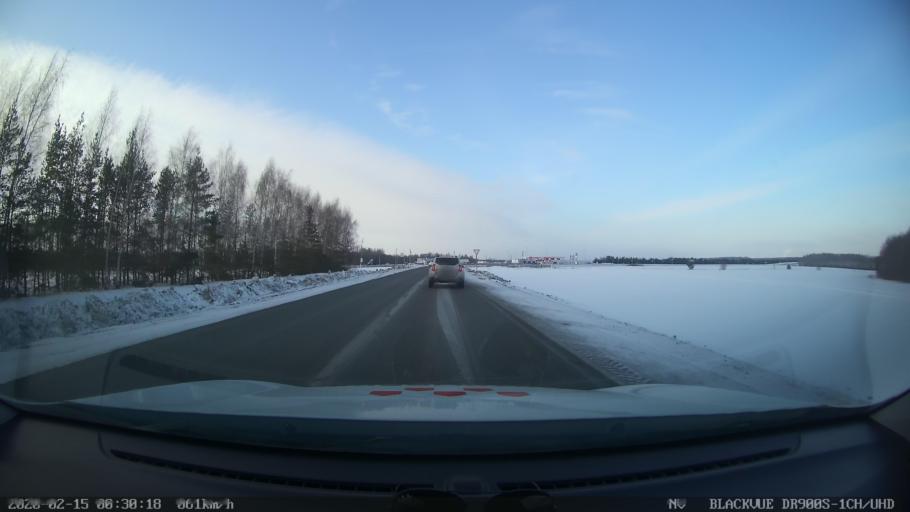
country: RU
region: Tatarstan
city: Verkhniy Uslon
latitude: 55.6579
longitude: 48.8592
